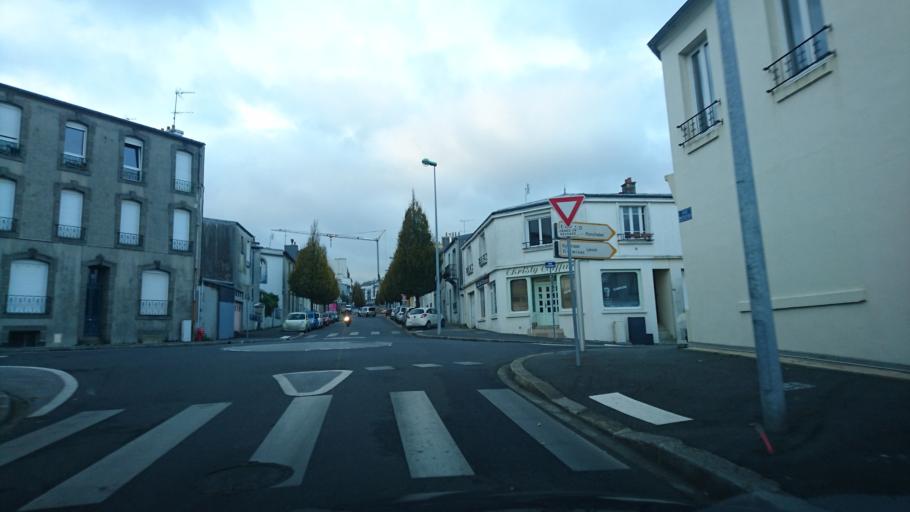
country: FR
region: Brittany
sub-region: Departement du Finistere
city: Brest
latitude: 48.3931
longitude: -4.4744
